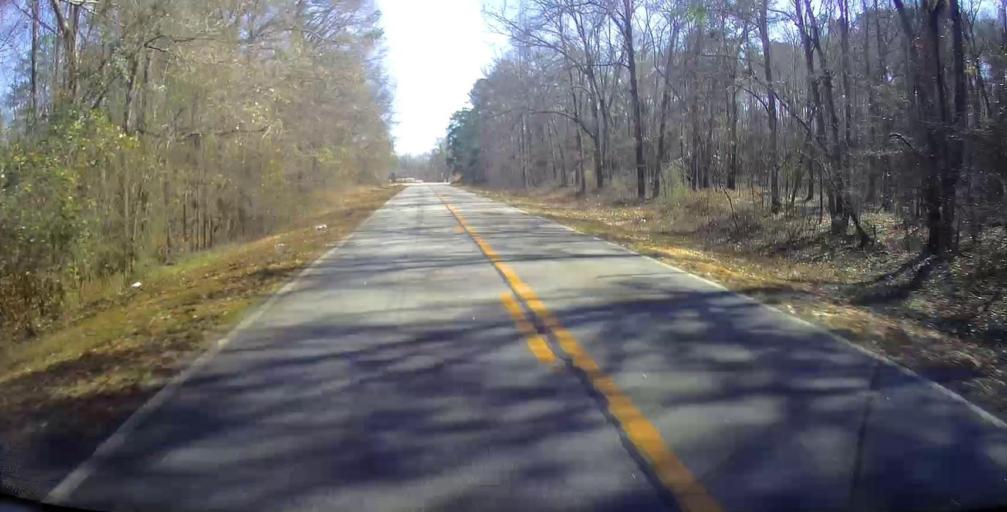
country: US
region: Georgia
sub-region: Peach County
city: Byron
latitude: 32.6037
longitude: -83.7995
